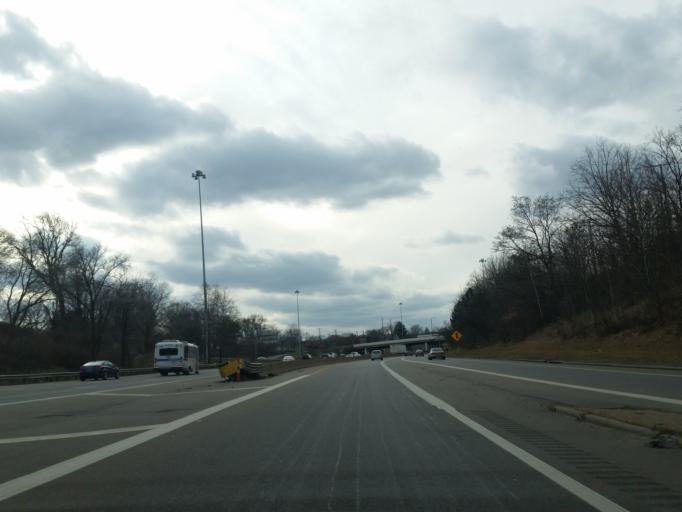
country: US
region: Ohio
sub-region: Cuyahoga County
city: Brooklyn Heights
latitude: 41.4585
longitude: -81.6970
